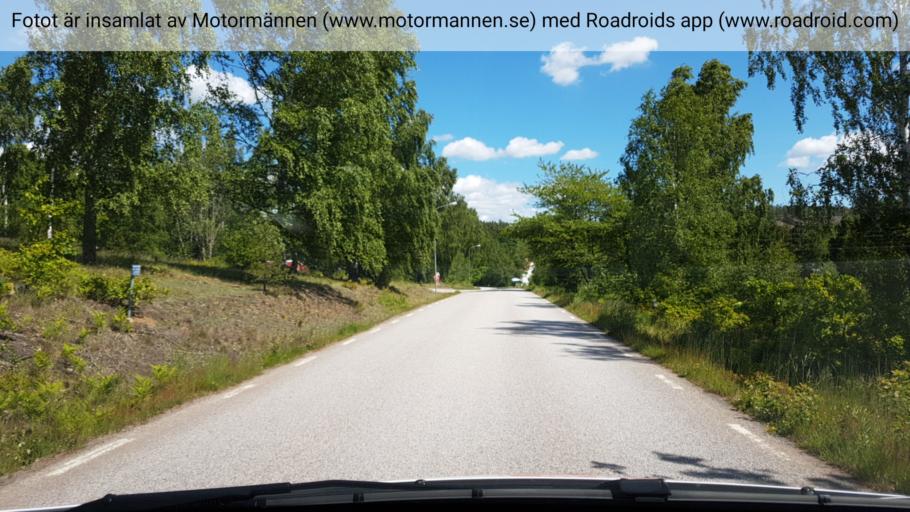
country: SE
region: Kalmar
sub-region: Vasterviks Kommun
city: Forserum
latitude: 57.9989
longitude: 16.4995
